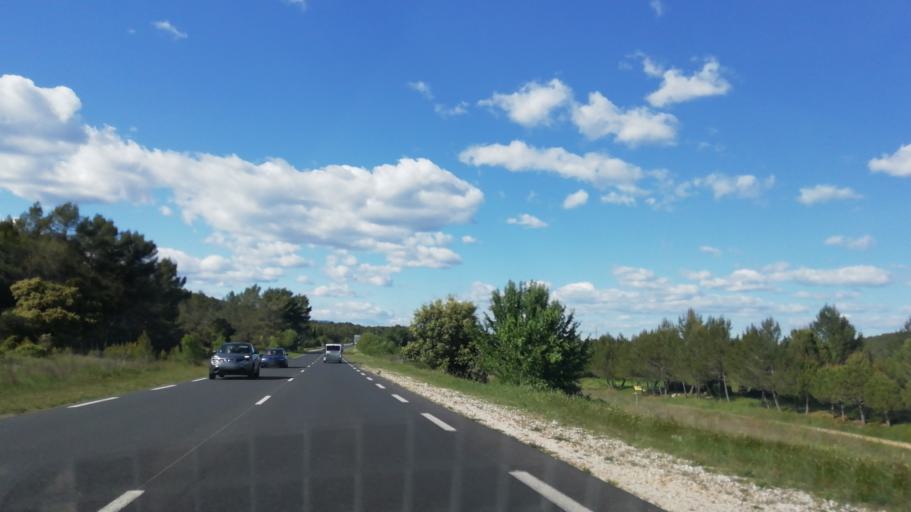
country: FR
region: Languedoc-Roussillon
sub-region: Departement de l'Herault
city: Saint-Clement-de-Riviere
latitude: 43.6821
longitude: 3.8216
